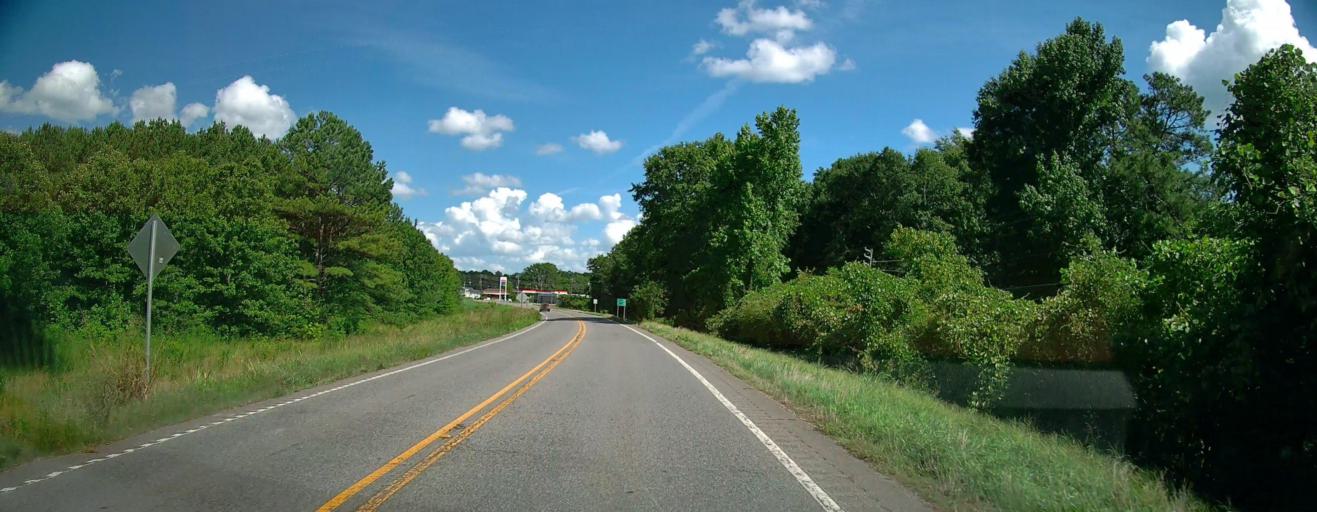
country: US
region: Alabama
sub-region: Pickens County
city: Gordo
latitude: 33.3189
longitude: -87.9077
